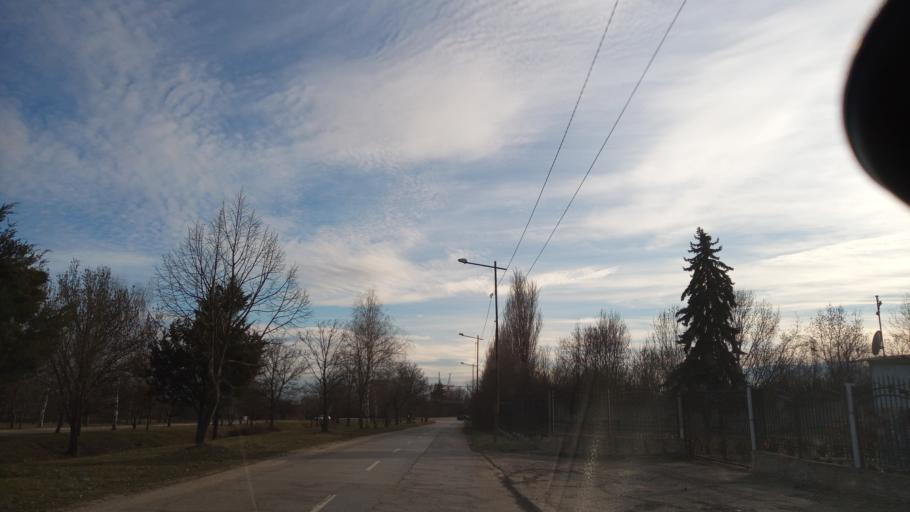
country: BG
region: Sofia-Capital
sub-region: Stolichna Obshtina
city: Bukhovo
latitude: 42.7572
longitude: 23.5601
